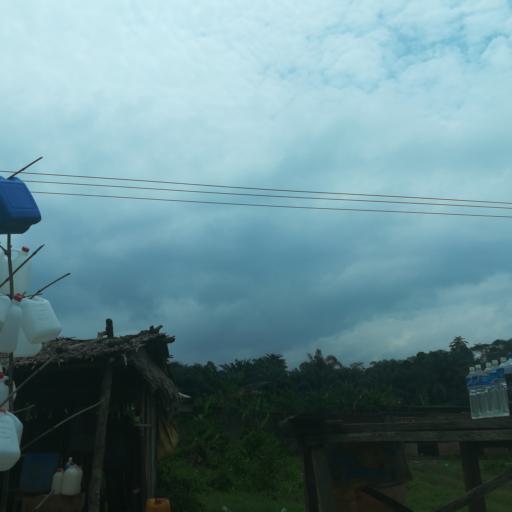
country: NG
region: Lagos
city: Ejirin
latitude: 6.6492
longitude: 3.7841
